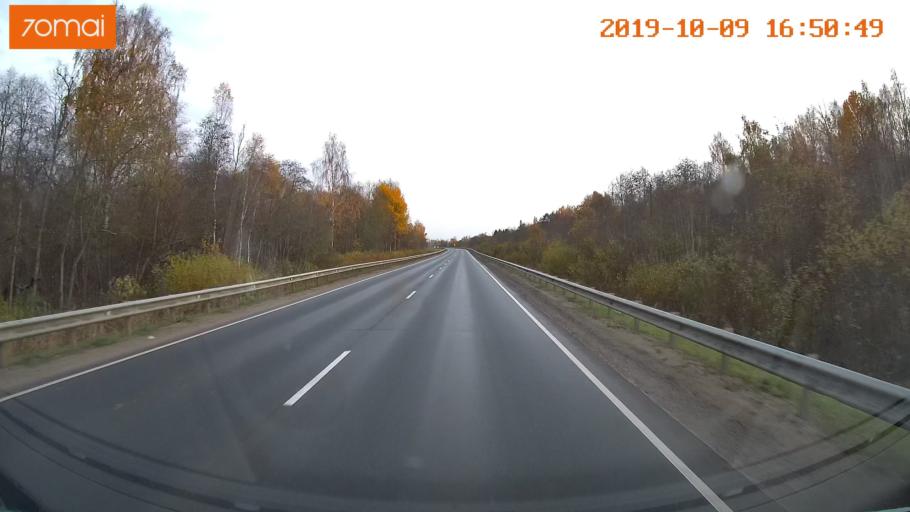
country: RU
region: Kostroma
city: Volgorechensk
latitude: 57.3956
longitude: 41.2138
